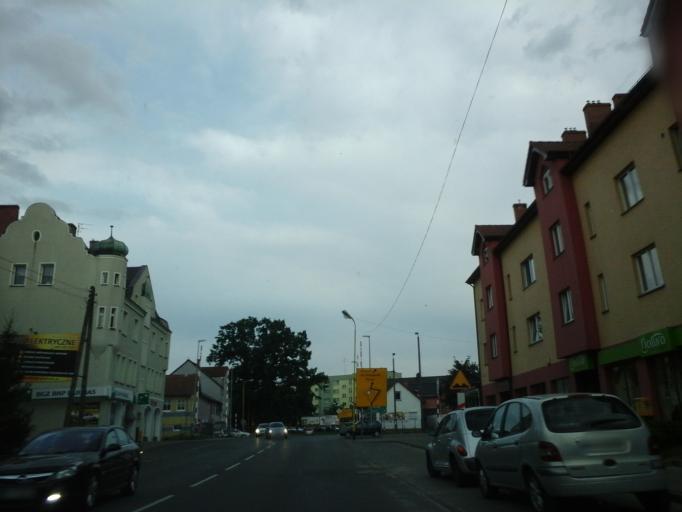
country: PL
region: West Pomeranian Voivodeship
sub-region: Powiat goleniowski
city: Nowogard
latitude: 53.6680
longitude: 15.1242
